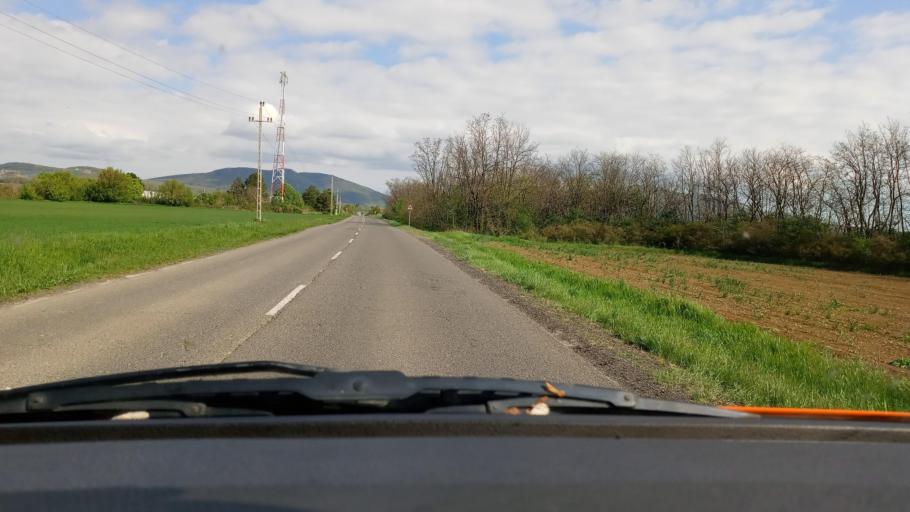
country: HU
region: Baranya
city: Hosszuheteny
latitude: 46.1234
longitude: 18.3487
